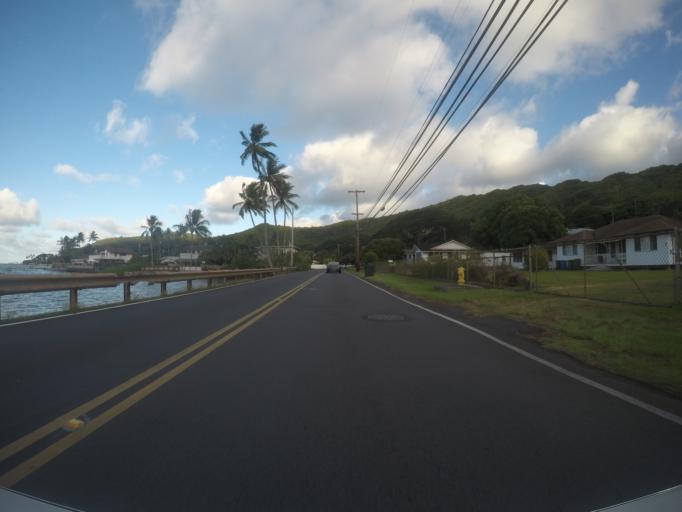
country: US
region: Hawaii
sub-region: Honolulu County
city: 'Ahuimanu
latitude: 21.4534
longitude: -157.8255
